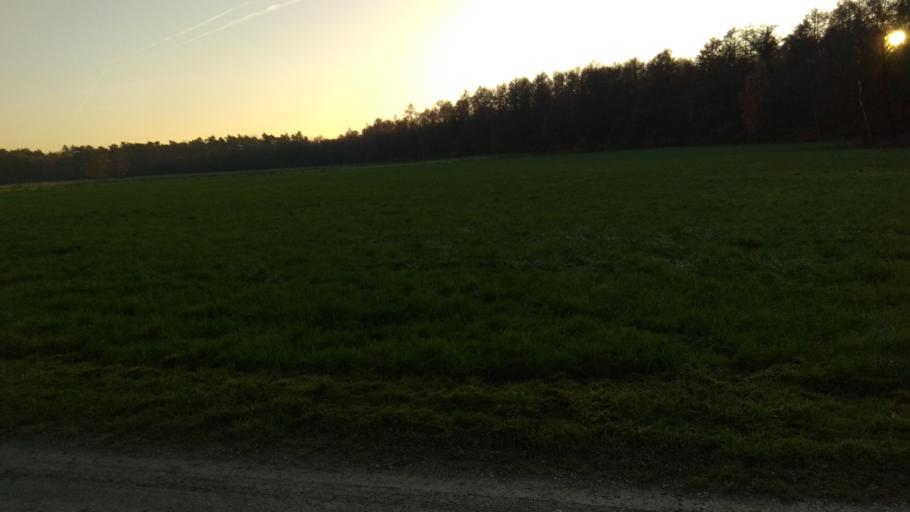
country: DE
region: North Rhine-Westphalia
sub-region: Regierungsbezirk Dusseldorf
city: Schermbeck
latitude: 51.6403
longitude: 6.8648
